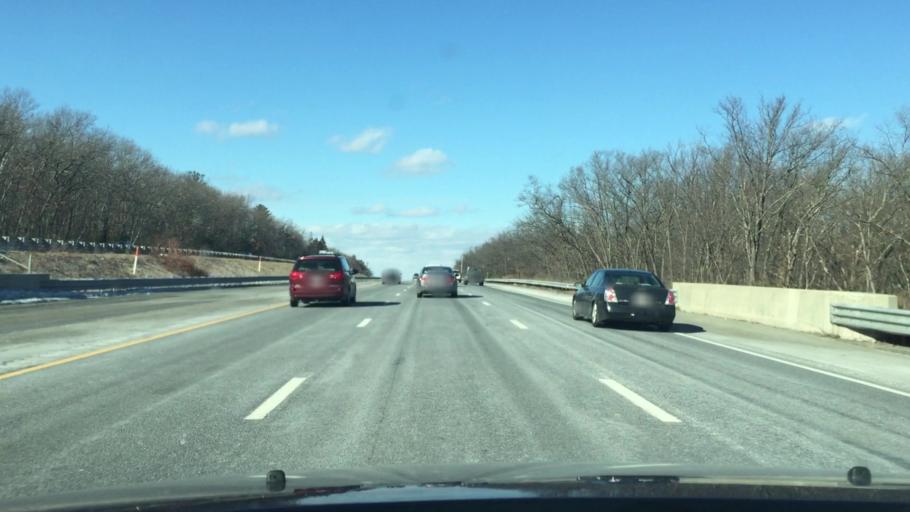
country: US
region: Massachusetts
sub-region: Middlesex County
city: Tyngsboro
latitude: 42.6438
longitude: -71.4156
